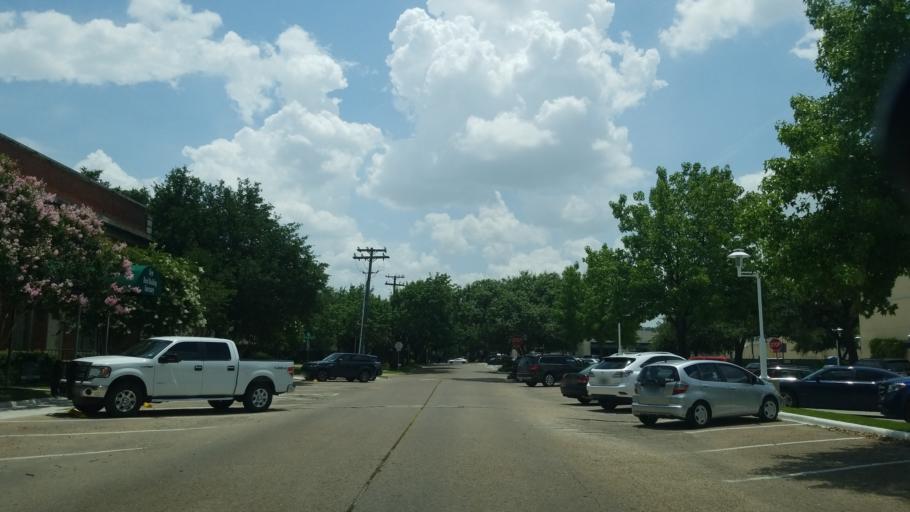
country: US
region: Texas
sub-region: Dallas County
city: University Park
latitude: 32.8650
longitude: -96.8019
